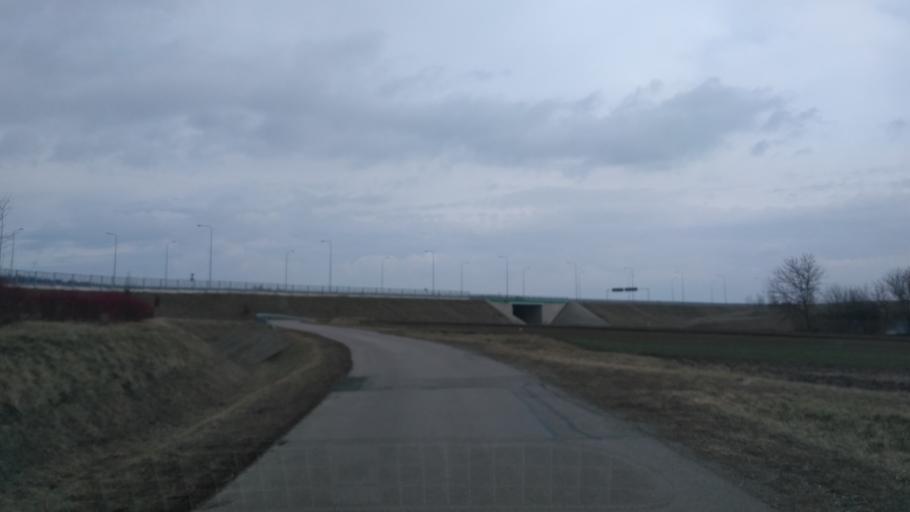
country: PL
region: Subcarpathian Voivodeship
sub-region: Powiat jaroslawski
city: Pawlosiow
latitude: 49.9696
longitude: 22.6463
